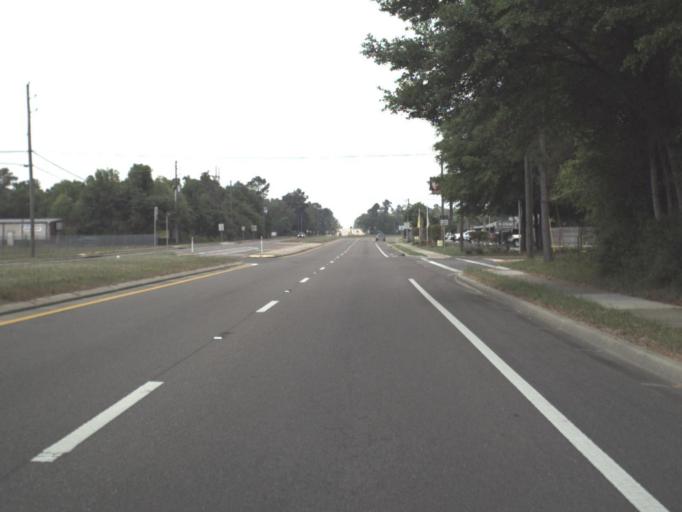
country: US
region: Florida
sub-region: Santa Rosa County
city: Point Baker
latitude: 30.6637
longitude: -87.0546
